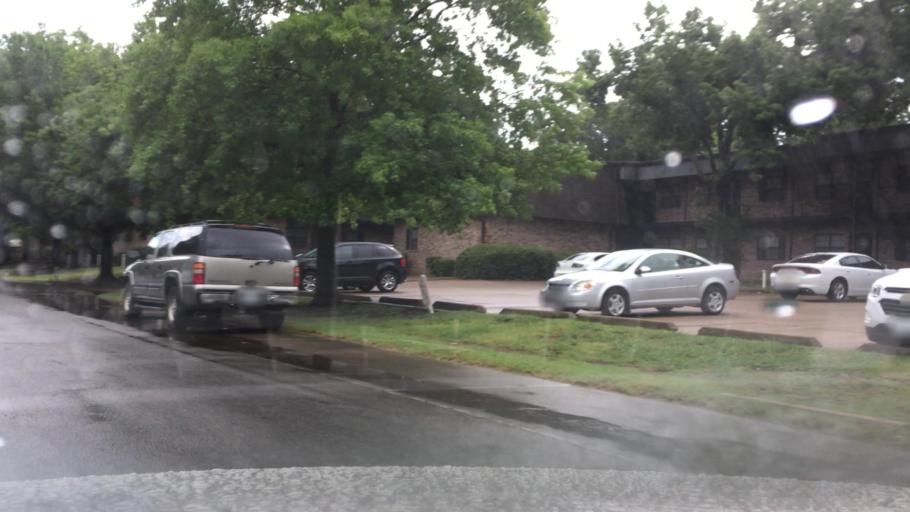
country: US
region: Oklahoma
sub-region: Cherokee County
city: Tahlequah
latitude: 35.9246
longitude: -94.9668
